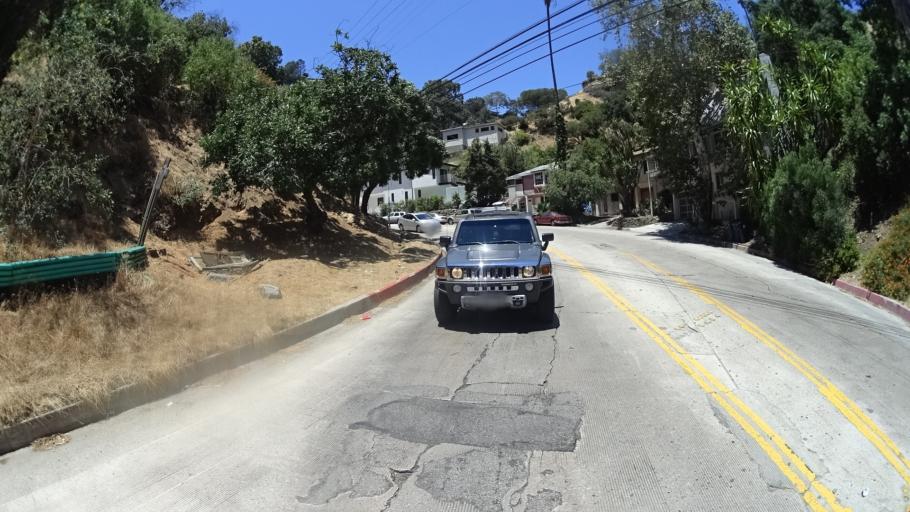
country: US
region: California
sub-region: Los Angeles County
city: West Hollywood
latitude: 34.1101
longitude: -118.3723
